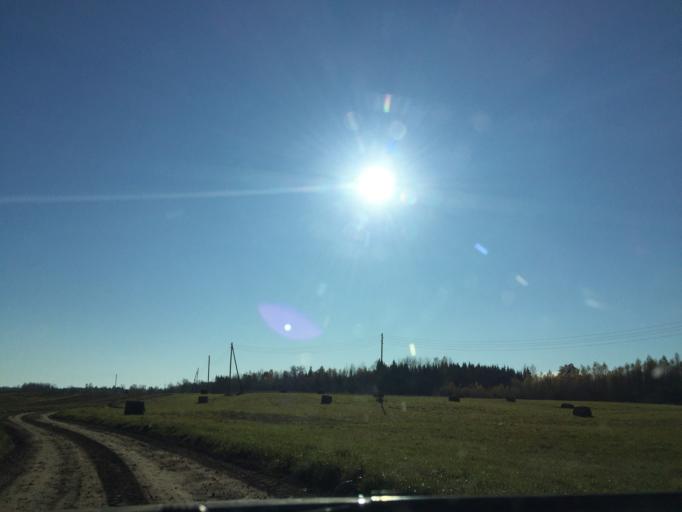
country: LV
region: Skriveri
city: Skriveri
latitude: 56.6598
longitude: 25.1848
